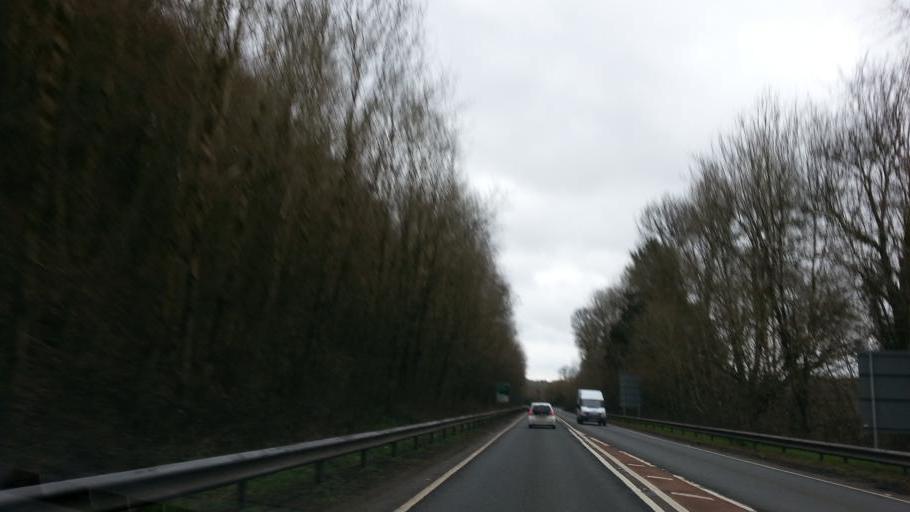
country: GB
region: England
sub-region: Devon
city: South Molton
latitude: 51.0145
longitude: -3.7665
